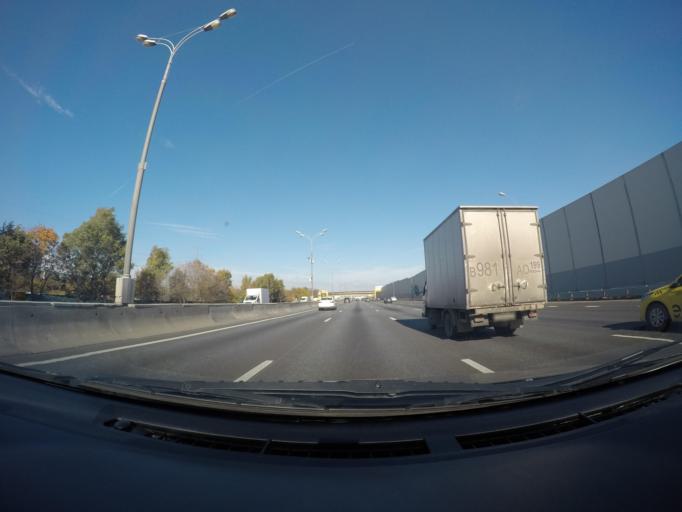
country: RU
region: Moskovskaya
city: Kuskovo
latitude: 55.7365
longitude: 37.8413
